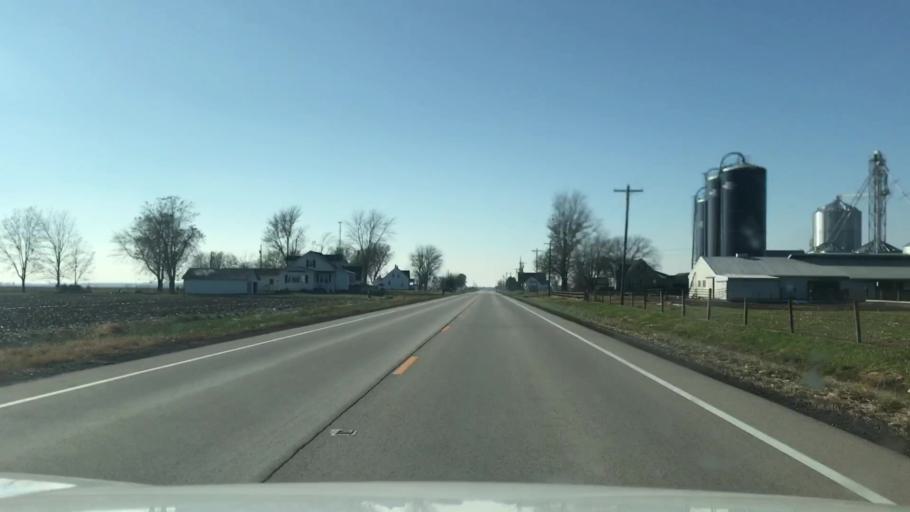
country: US
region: Illinois
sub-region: Washington County
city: Okawville
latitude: 38.4421
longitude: -89.4849
